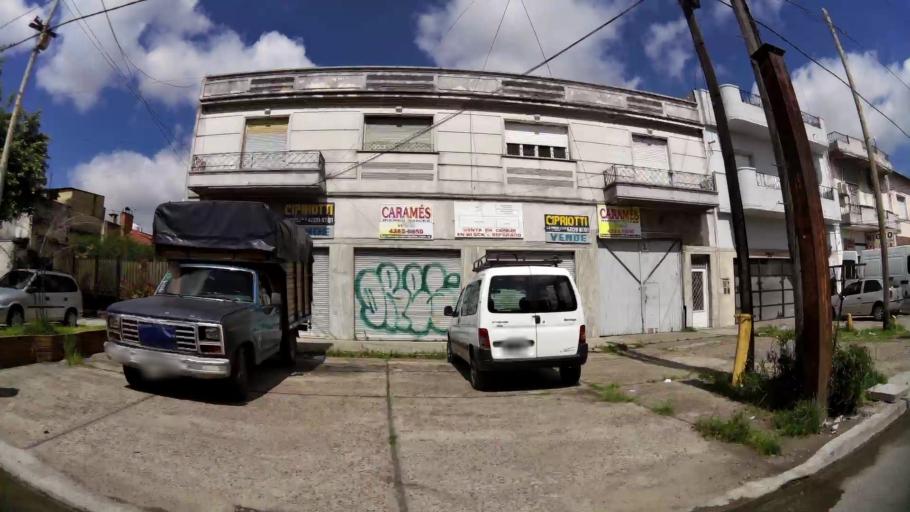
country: AR
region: Buenos Aires
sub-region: Partido de Lanus
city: Lanus
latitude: -34.6850
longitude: -58.4185
